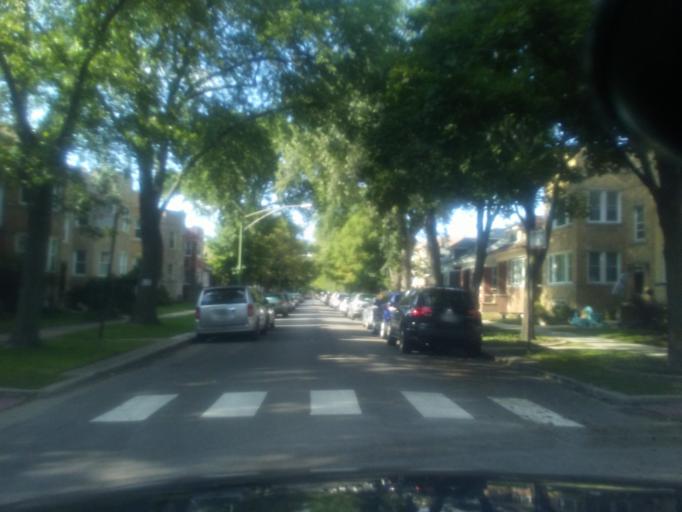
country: US
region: Illinois
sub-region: Cook County
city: Lincolnwood
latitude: 41.9850
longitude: -87.6931
